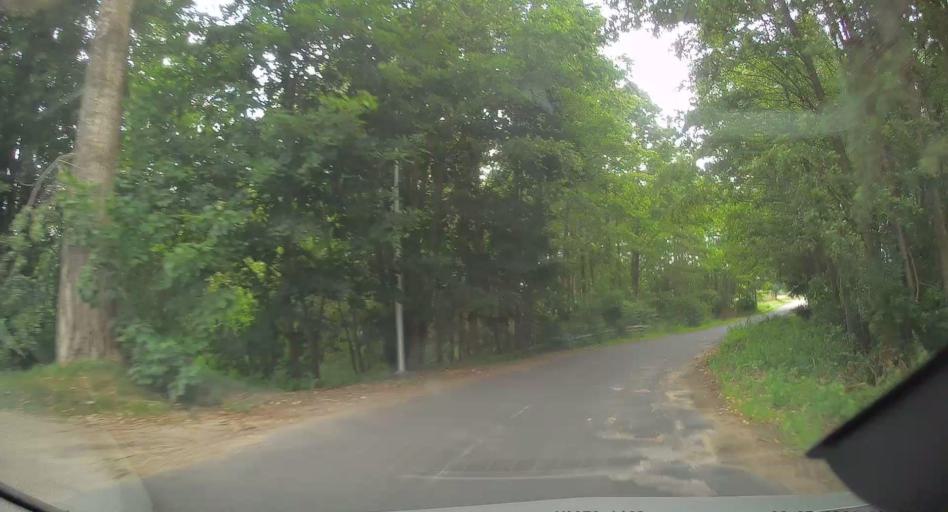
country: PL
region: Lodz Voivodeship
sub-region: Powiat rawski
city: Rawa Mazowiecka
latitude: 51.7393
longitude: 20.1908
